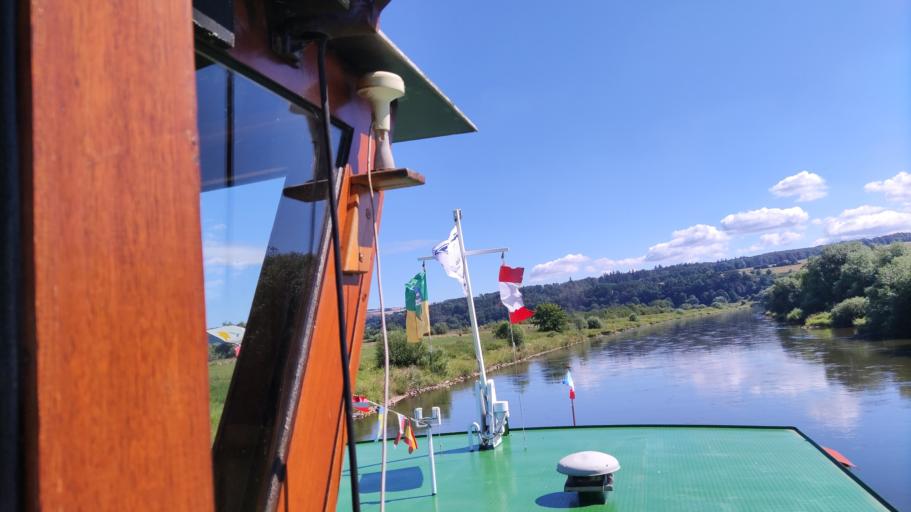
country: DE
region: North Rhine-Westphalia
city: Beverungen
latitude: 51.6700
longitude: 9.3851
